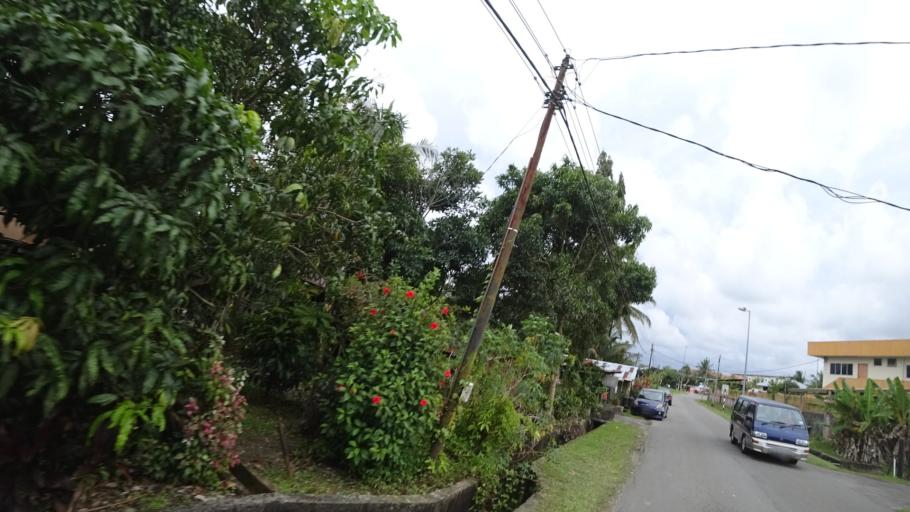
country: BN
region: Brunei and Muara
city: Bandar Seri Begawan
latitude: 4.8524
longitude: 114.8451
